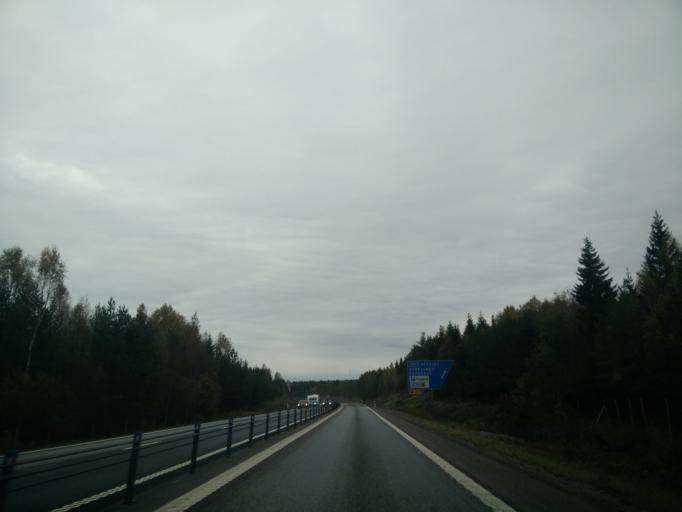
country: SE
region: Gaevleborg
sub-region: Gavle Kommun
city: Norrsundet
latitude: 60.9080
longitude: 17.0146
